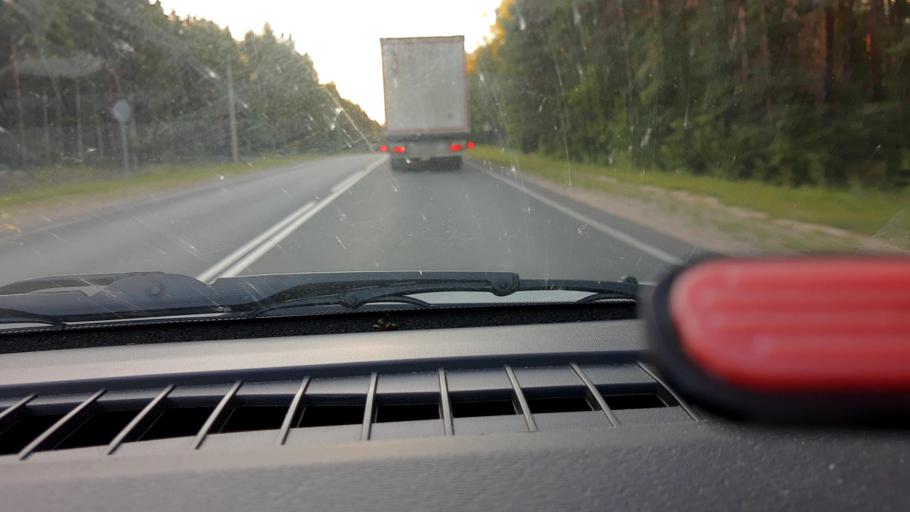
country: RU
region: Nizjnij Novgorod
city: Uren'
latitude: 57.3550
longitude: 45.7020
